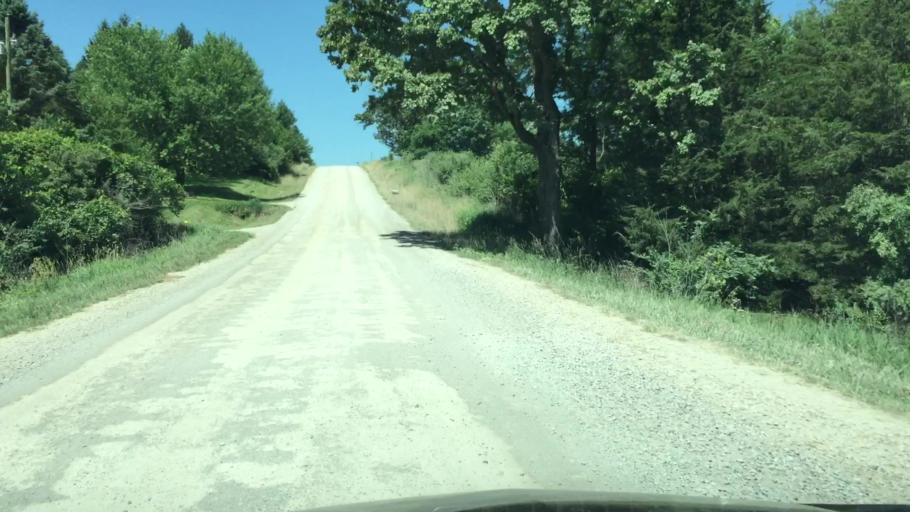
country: US
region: Iowa
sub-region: Linn County
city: Ely
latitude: 41.8328
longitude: -91.5754
